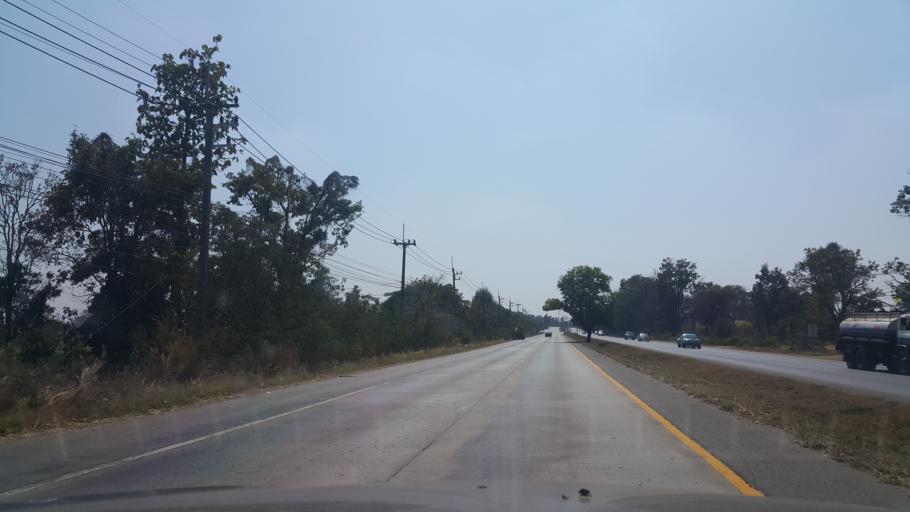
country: TH
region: Khon Kaen
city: Nam Phong
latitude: 16.7864
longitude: 102.8260
